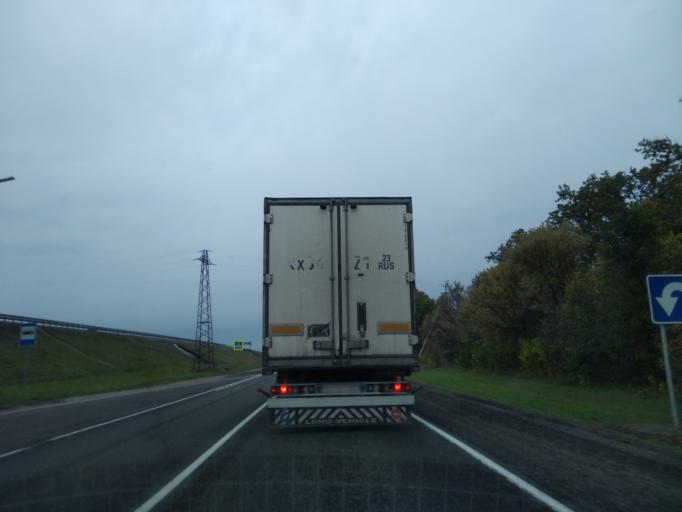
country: RU
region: Lipetsk
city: Zadonsk
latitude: 52.4590
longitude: 38.7762
